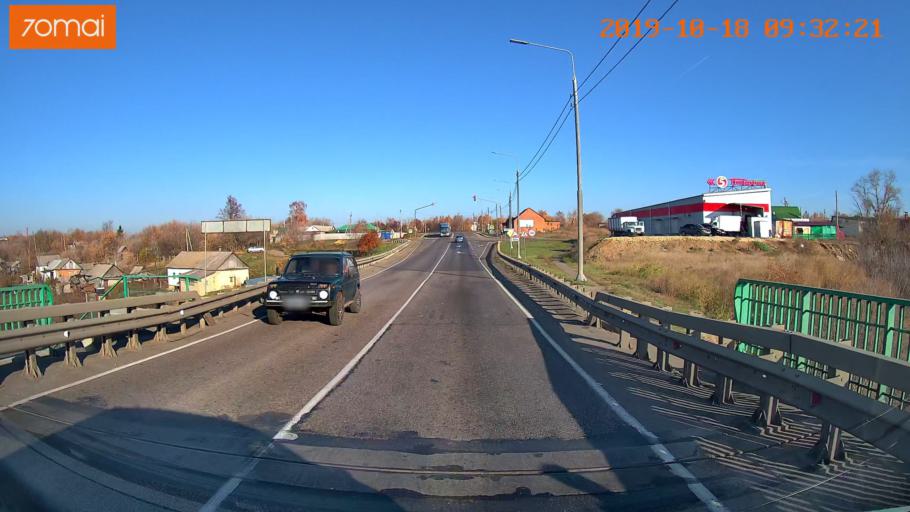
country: RU
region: Tula
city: Yefremov
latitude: 53.1598
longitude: 38.1555
